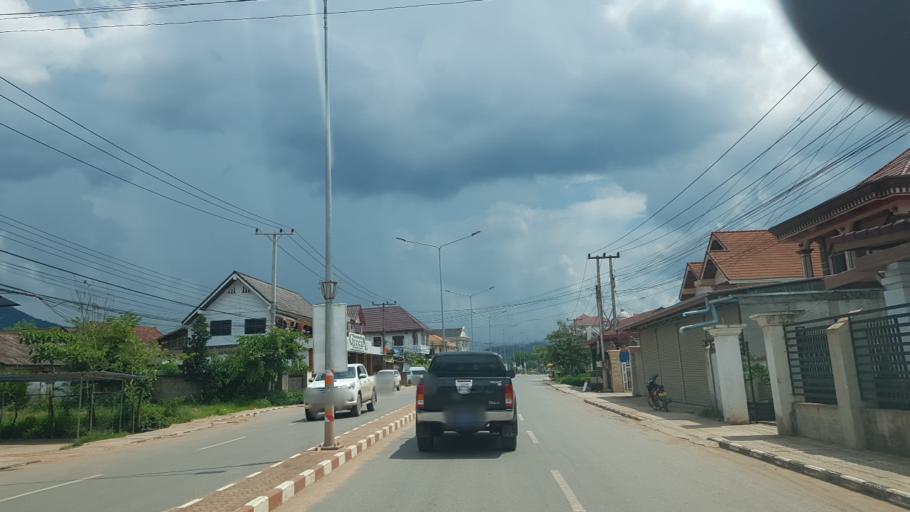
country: LA
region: Oudomxai
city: Muang Xay
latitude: 20.6777
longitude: 101.9867
